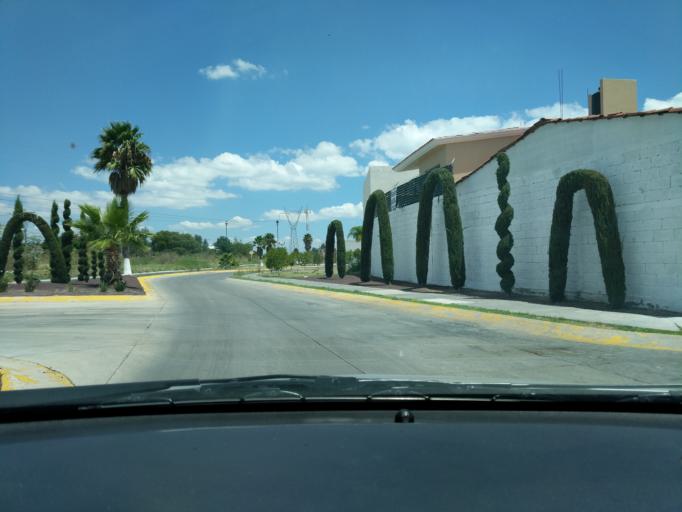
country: MX
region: Guanajuato
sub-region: Salamanca
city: El Divisador
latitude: 20.5994
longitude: -101.1727
